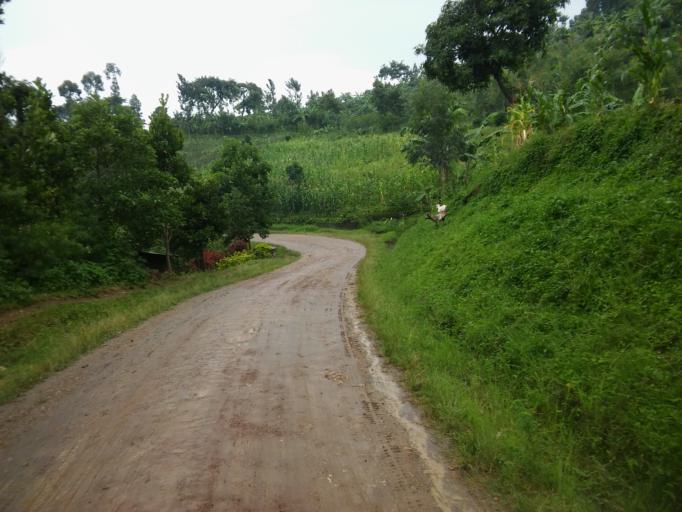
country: UG
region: Eastern Region
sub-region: Mbale District
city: Mbale
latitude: 1.0149
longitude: 34.2272
